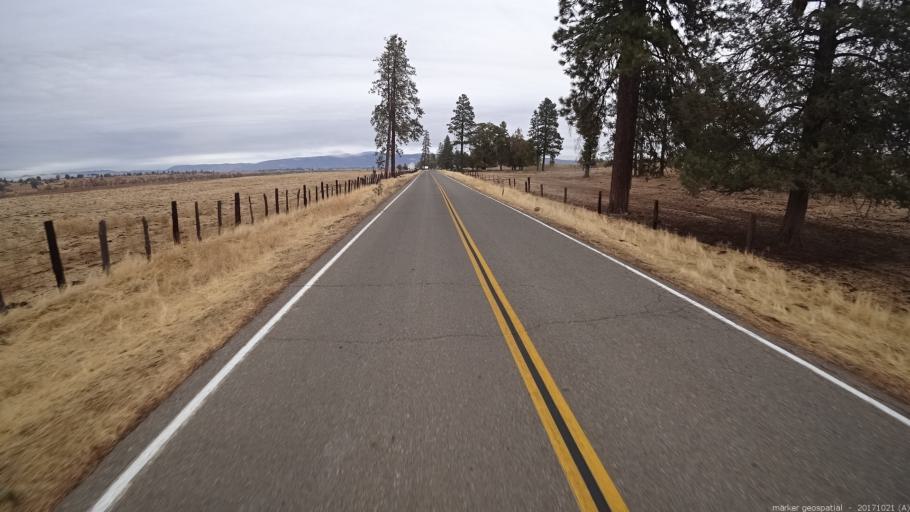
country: US
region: California
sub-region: Shasta County
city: Burney
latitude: 41.0149
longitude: -121.4169
